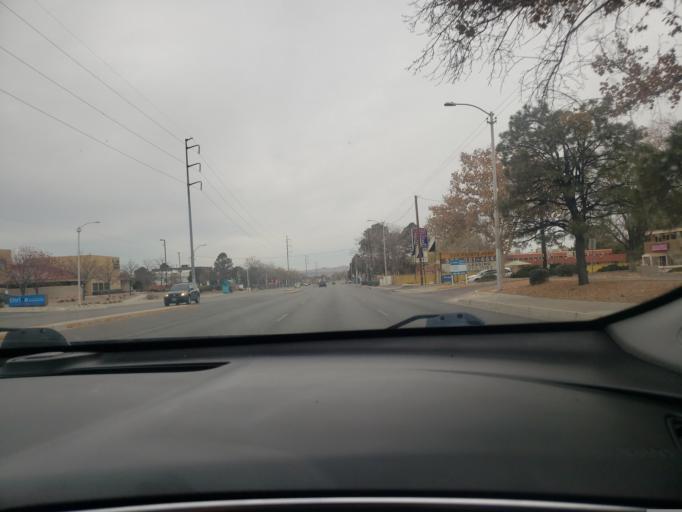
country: US
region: New Mexico
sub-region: Bernalillo County
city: North Valley
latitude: 35.1310
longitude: -106.5979
